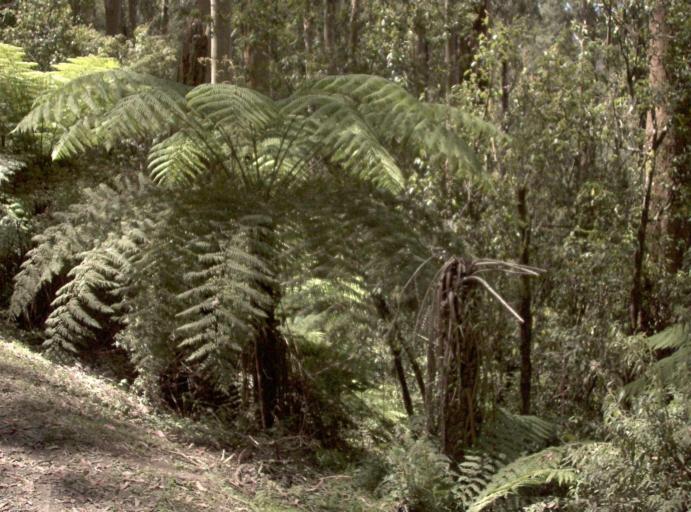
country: AU
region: Victoria
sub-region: Yarra Ranges
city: Millgrove
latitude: -37.6825
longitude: 145.7226
